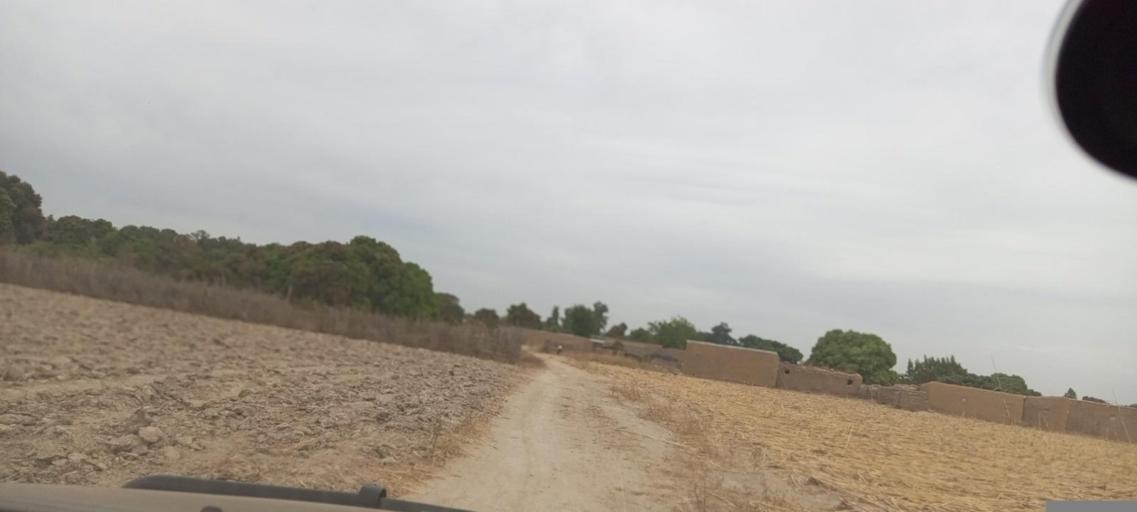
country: ML
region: Koulikoro
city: Kati
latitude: 12.7414
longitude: -8.3294
